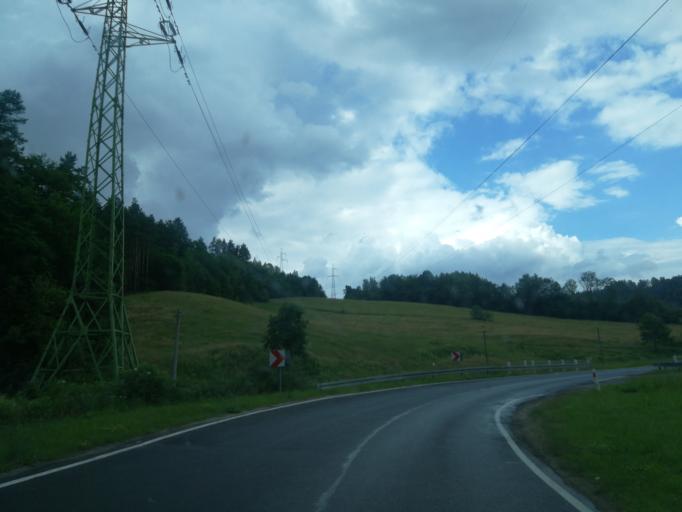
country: PL
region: Subcarpathian Voivodeship
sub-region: Powiat leski
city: Olszanica
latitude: 49.4264
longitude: 22.4539
